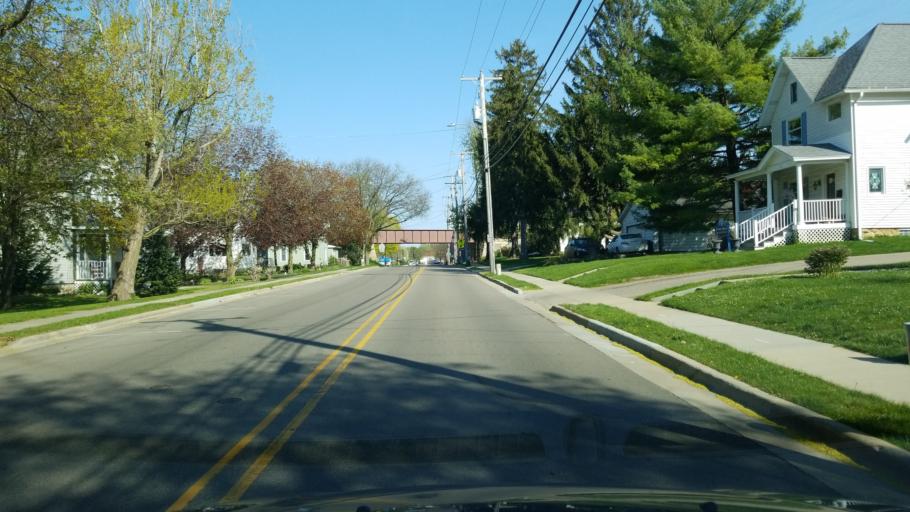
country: US
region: Wisconsin
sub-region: Dane County
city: Oregon
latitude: 42.9274
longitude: -89.3878
